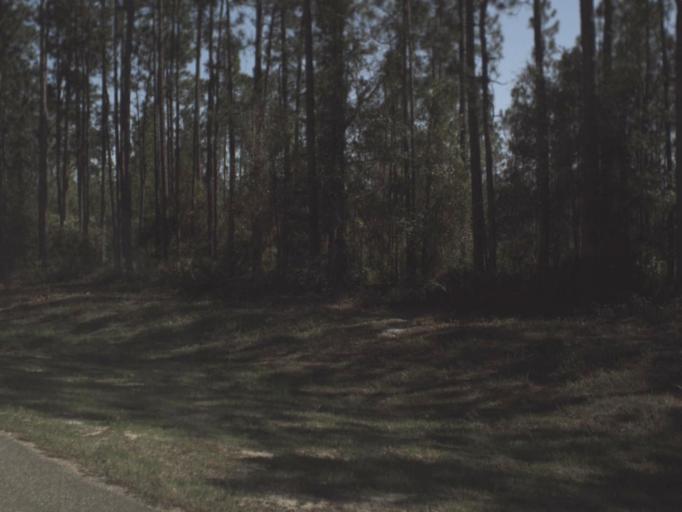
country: US
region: Florida
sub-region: Liberty County
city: Bristol
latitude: 30.4142
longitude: -84.8617
